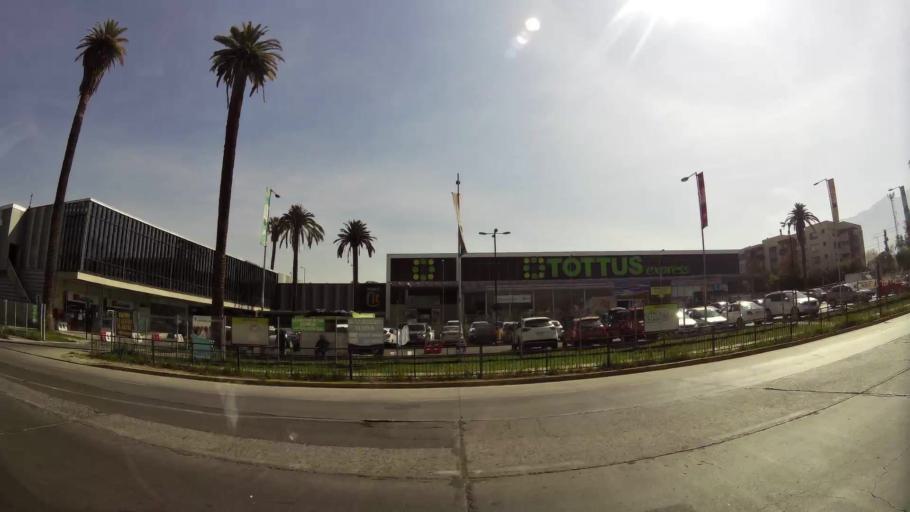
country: CL
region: Santiago Metropolitan
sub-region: Provincia de Santiago
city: Villa Presidente Frei, Nunoa, Santiago, Chile
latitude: -33.5223
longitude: -70.5584
